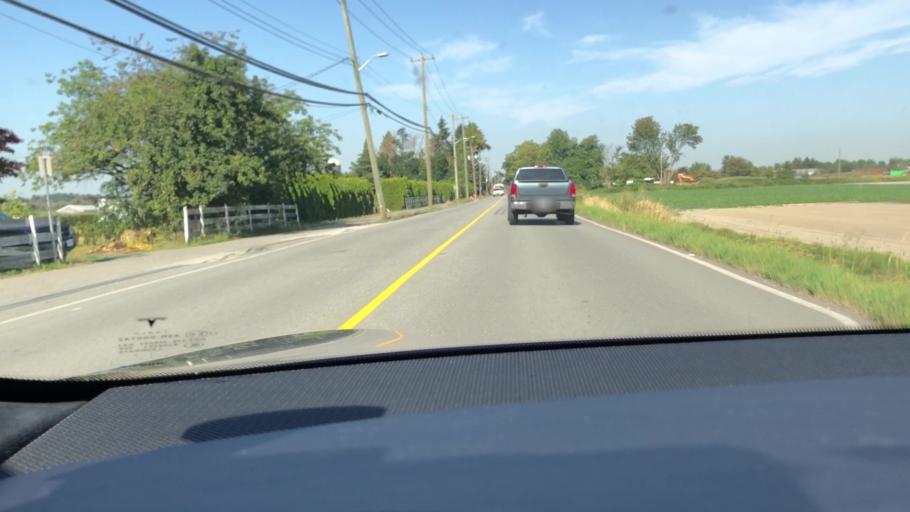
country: CA
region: British Columbia
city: Richmond
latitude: 49.1696
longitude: -123.0550
